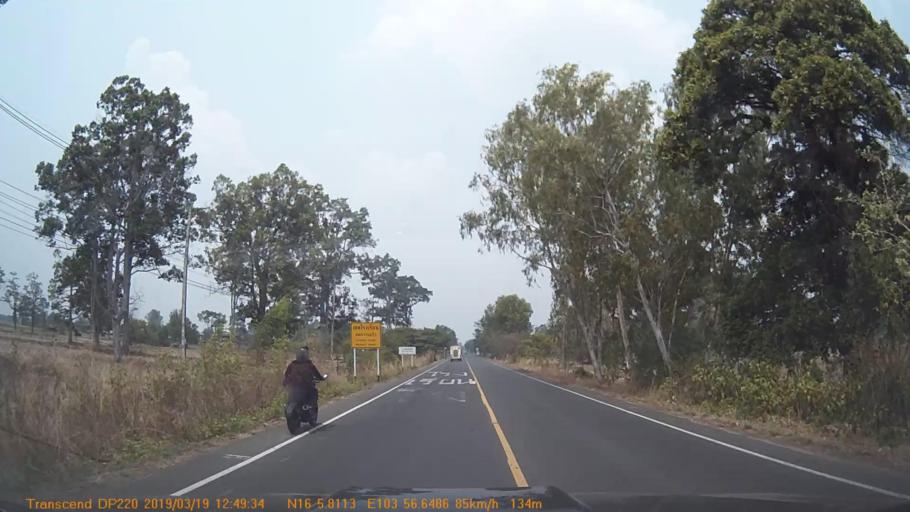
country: TH
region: Roi Et
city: Selaphum
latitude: 16.0973
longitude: 103.9442
